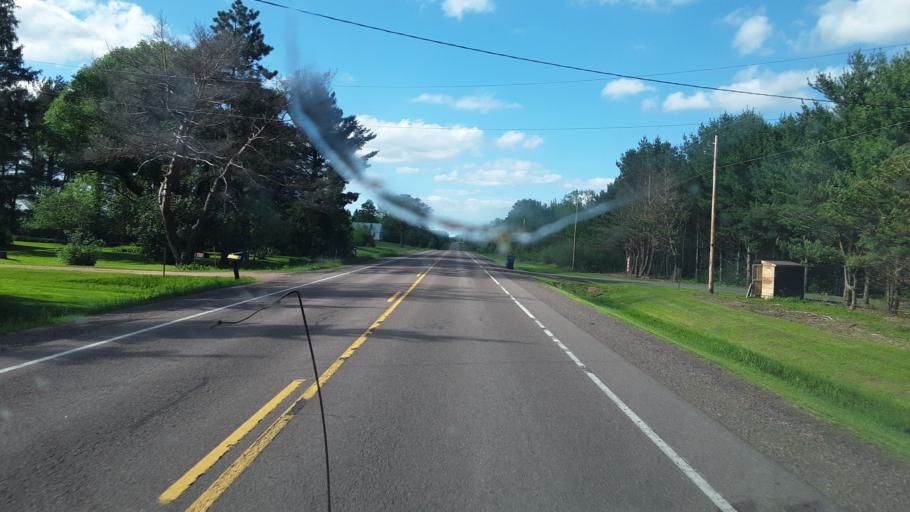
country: US
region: Wisconsin
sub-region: Wood County
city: Marshfield
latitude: 44.5040
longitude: -90.1801
